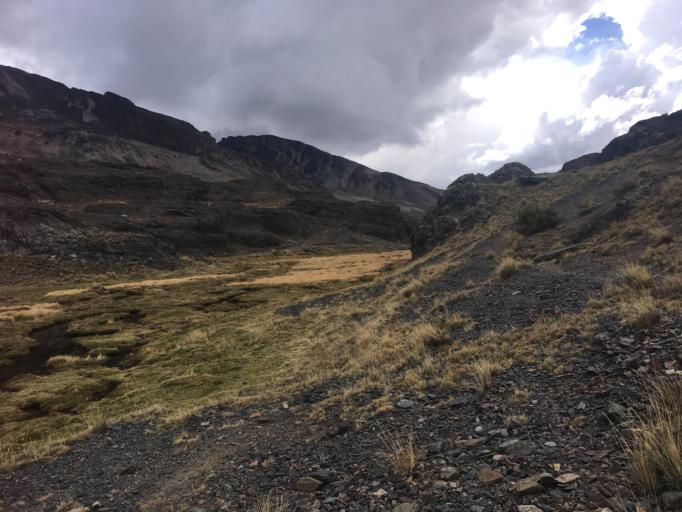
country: BO
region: La Paz
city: La Paz
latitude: -16.3948
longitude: -67.9716
